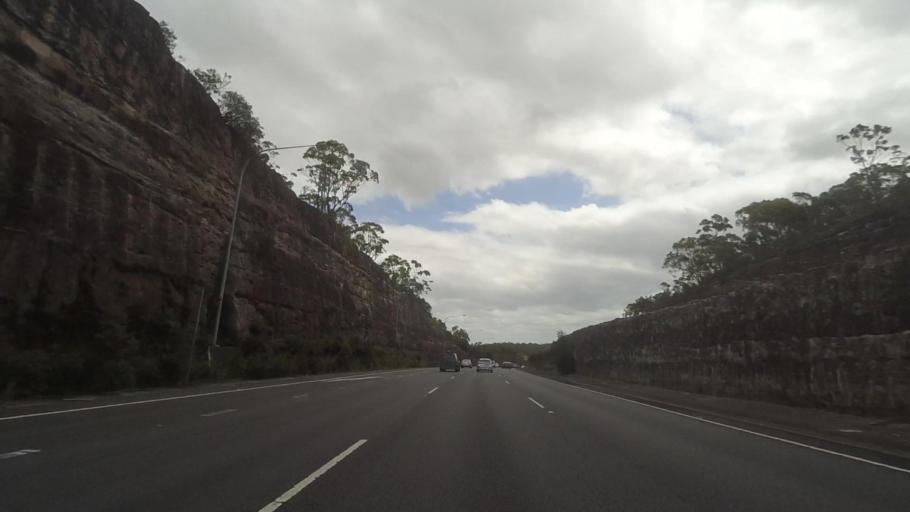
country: AU
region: New South Wales
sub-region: Gosford Shire
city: Point Clare
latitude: -33.4575
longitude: 151.2035
